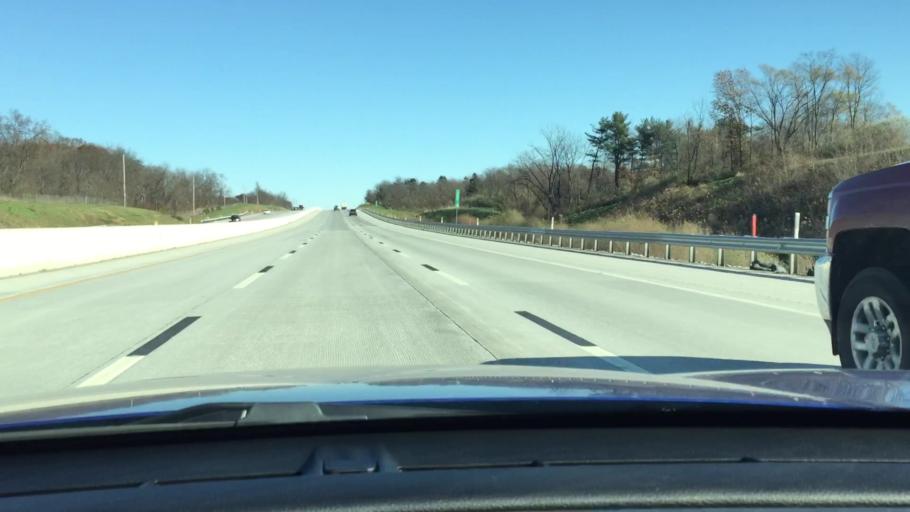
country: US
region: Pennsylvania
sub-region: Cumberland County
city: Newville
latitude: 40.1805
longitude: -77.5029
